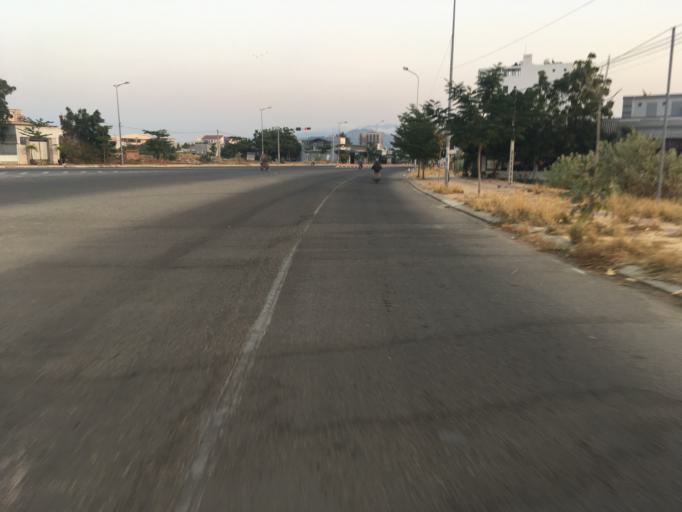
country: VN
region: Ninh Thuan
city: Phan Rang-Thap Cham
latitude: 11.5588
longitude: 109.0215
